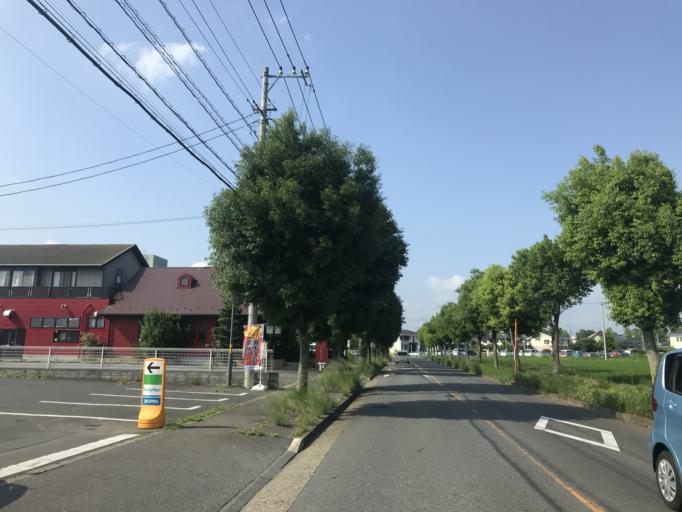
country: JP
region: Ibaraki
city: Naka
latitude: 36.0679
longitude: 140.0958
